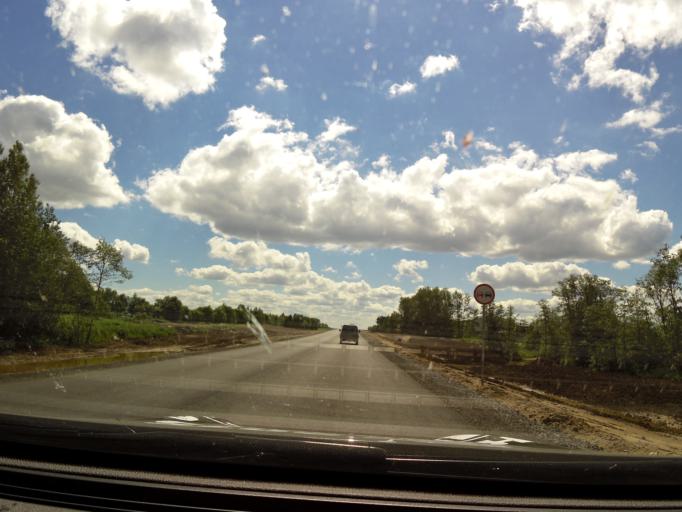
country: RU
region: Vologda
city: Molochnoye
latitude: 59.3098
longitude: 39.6857
